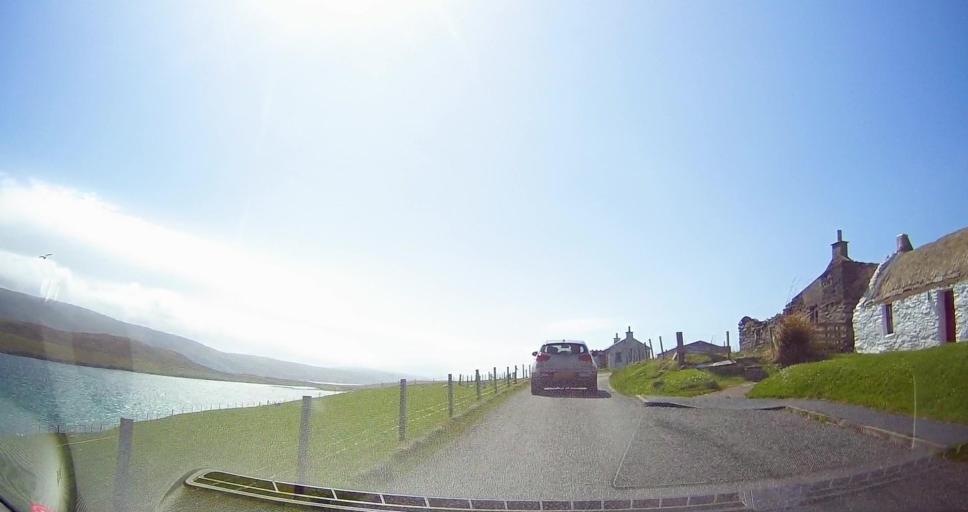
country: GB
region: Scotland
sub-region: Shetland Islands
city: Sandwick
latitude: 60.0625
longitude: -1.3402
